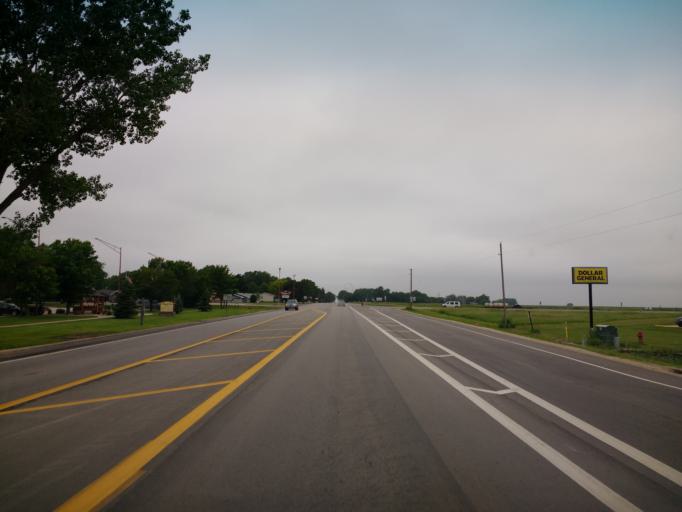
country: US
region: Iowa
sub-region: O'Brien County
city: Sanborn
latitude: 43.1861
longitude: -95.6421
